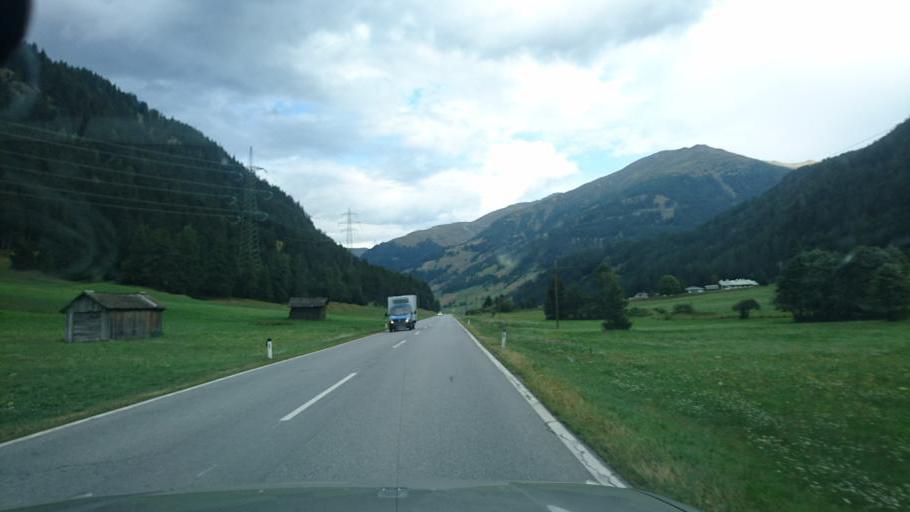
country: AT
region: Tyrol
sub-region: Politischer Bezirk Landeck
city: Nauders
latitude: 46.8559
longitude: 10.5061
